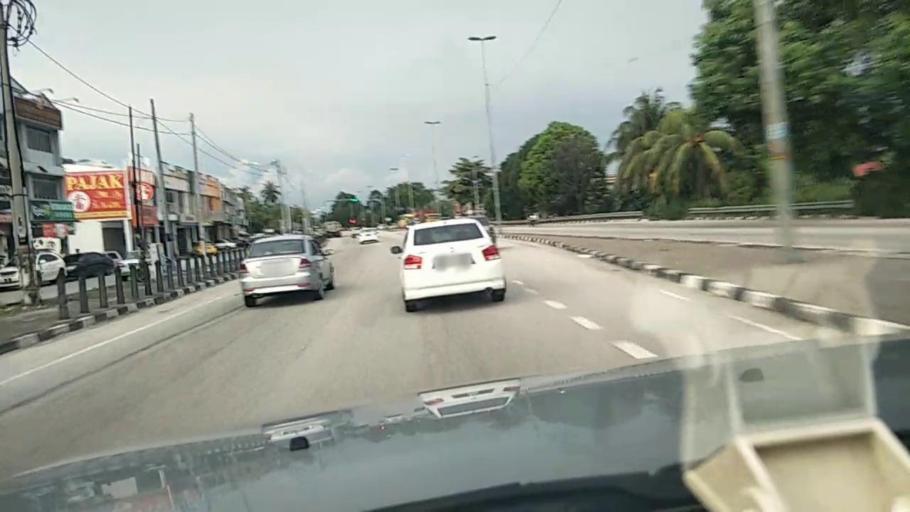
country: MY
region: Perak
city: Kampong Dungun
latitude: 3.1310
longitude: 101.3753
